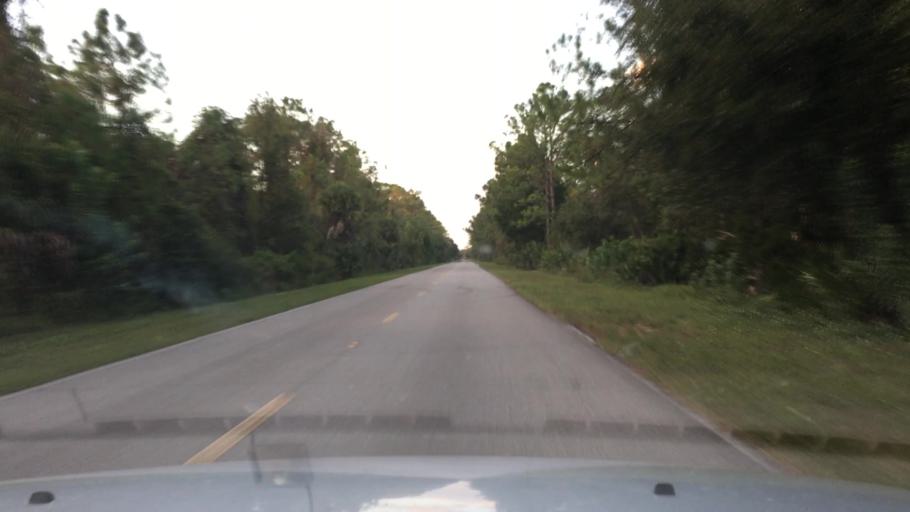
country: US
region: Florida
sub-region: Volusia County
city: Ormond Beach
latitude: 29.2897
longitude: -81.1268
